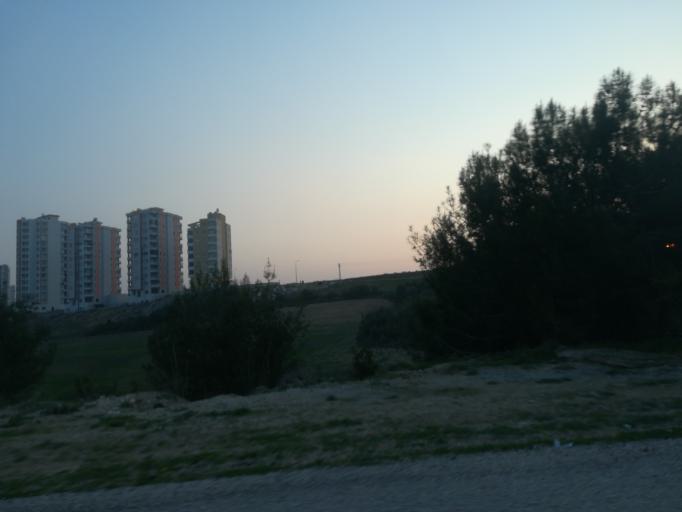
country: TR
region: Adana
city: Adana
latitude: 37.0811
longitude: 35.4114
